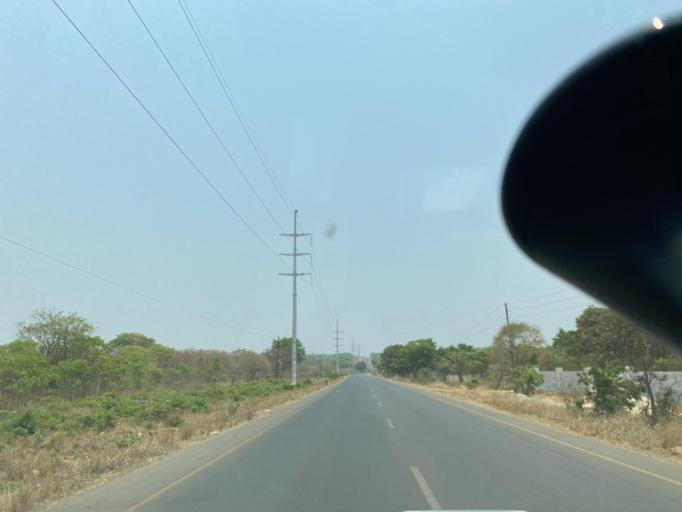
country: ZM
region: Lusaka
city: Lusaka
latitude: -15.5234
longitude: 28.4604
